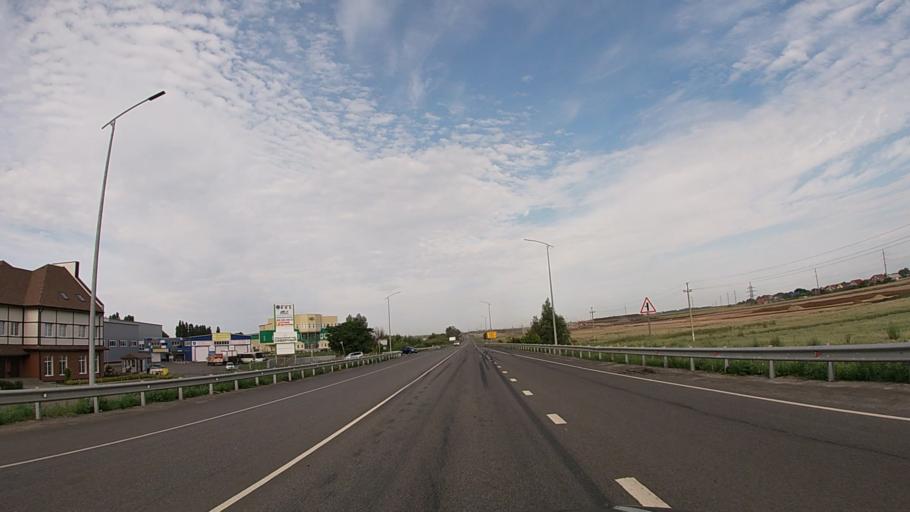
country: RU
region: Belgorod
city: Severnyy
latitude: 50.6674
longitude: 36.5539
